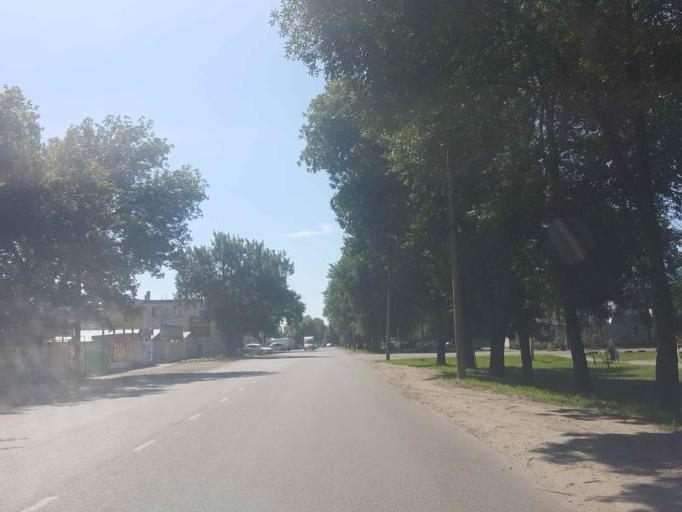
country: RU
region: Tambov
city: Tambov
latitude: 52.7177
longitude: 41.4243
